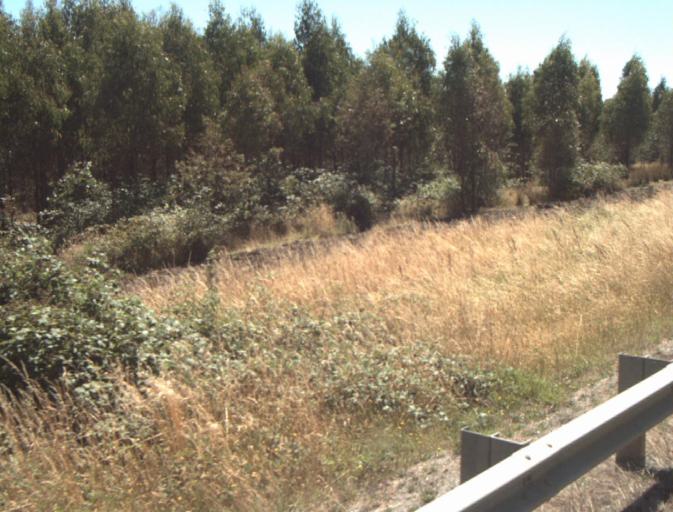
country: AU
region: Tasmania
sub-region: Launceston
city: Newstead
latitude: -41.3858
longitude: 147.3080
